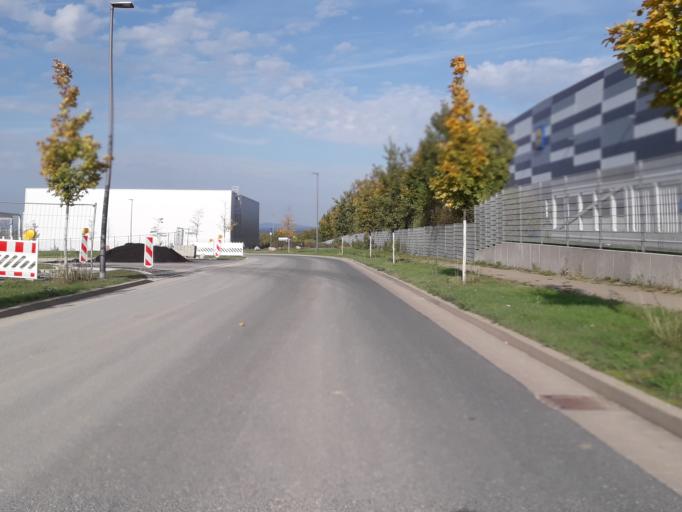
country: DE
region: North Rhine-Westphalia
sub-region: Regierungsbezirk Detmold
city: Paderborn
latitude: 51.6867
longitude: 8.7287
